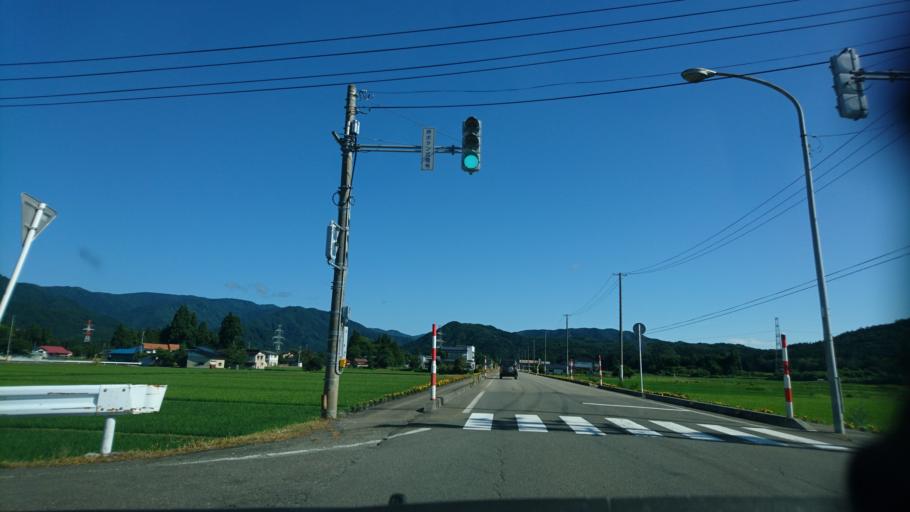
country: JP
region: Akita
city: Kakunodatemachi
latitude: 39.6596
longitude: 140.5700
